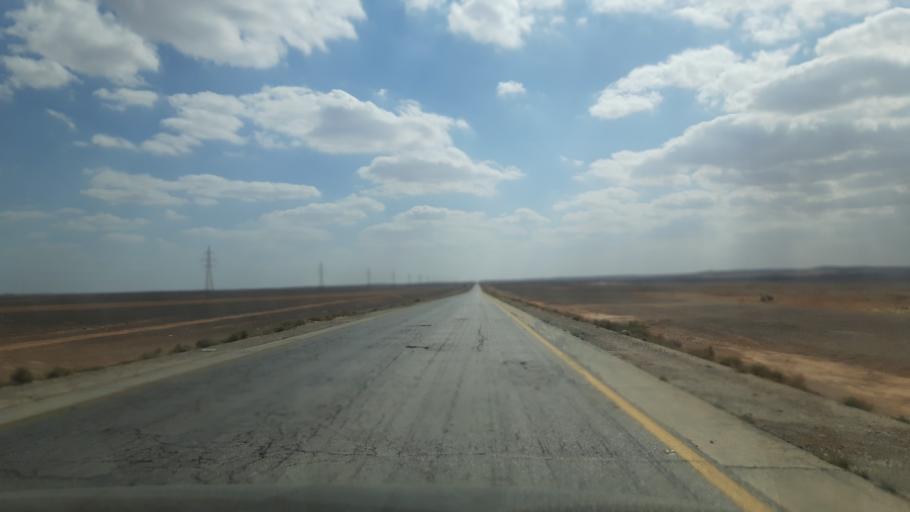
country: JO
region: Amman
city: Al Azraq ash Shamali
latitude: 31.7803
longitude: 36.5732
